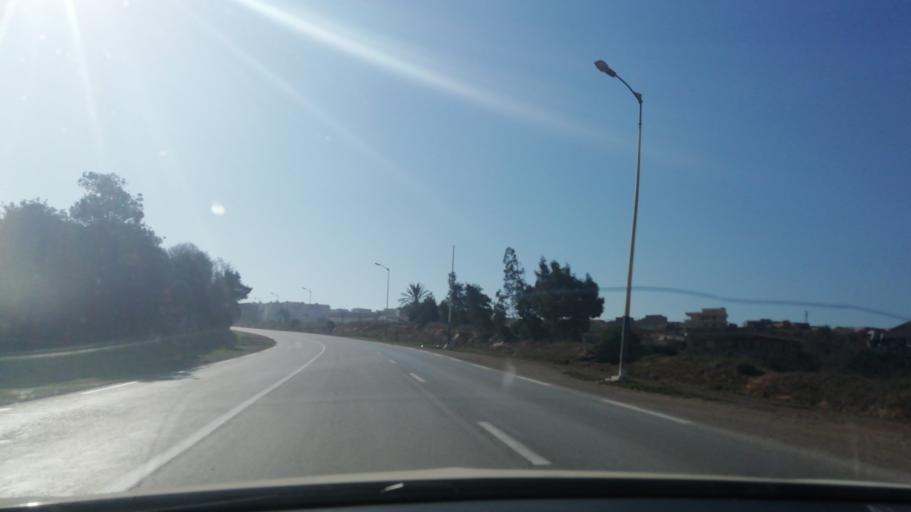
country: DZ
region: Tlemcen
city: Nedroma
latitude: 35.1027
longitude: -1.8338
